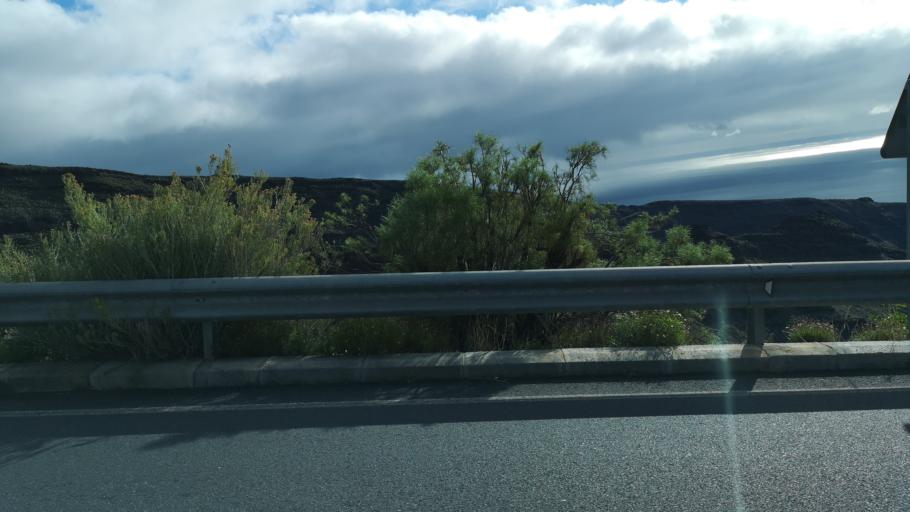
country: ES
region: Canary Islands
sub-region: Provincia de Santa Cruz de Tenerife
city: Alajero
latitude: 28.0633
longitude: -17.2036
